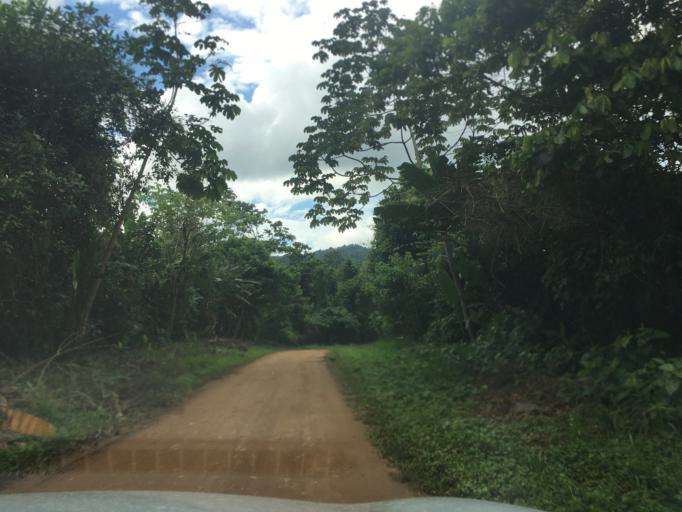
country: BZ
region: Stann Creek
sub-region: Dangriga
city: Dangriga
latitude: 16.9332
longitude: -88.3793
